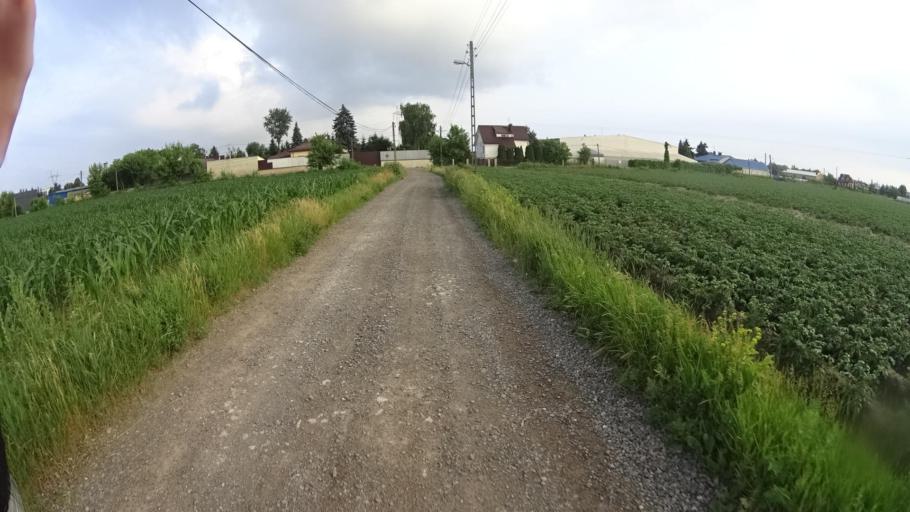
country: PL
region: Masovian Voivodeship
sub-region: Powiat warszawski zachodni
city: Babice
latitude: 52.2178
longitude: 20.8550
